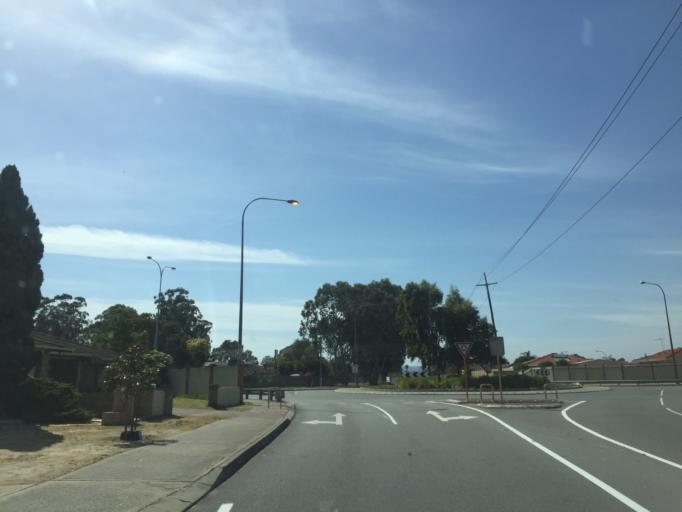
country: AU
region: Western Australia
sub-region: Gosnells
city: Thornlie
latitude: -32.0748
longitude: 115.9608
